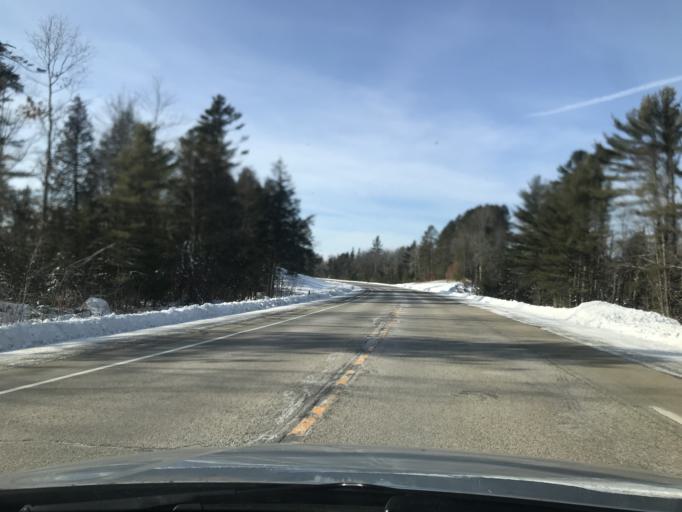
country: US
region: Wisconsin
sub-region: Oconto County
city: Gillett
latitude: 45.1274
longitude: -88.4045
